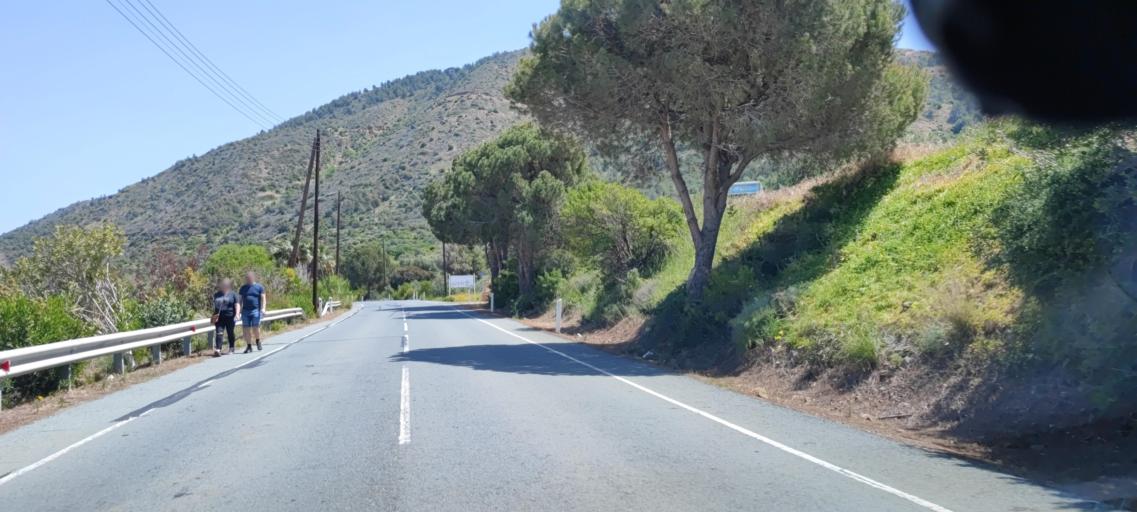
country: CY
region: Lefkosia
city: Kato Pyrgos
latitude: 35.1687
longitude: 32.5623
